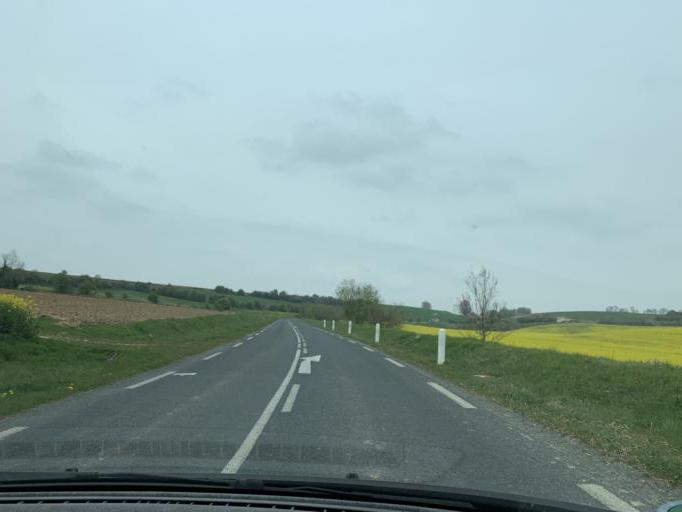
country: FR
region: Haute-Normandie
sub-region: Departement de la Seine-Maritime
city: Londinieres
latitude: 49.8398
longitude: 1.4547
